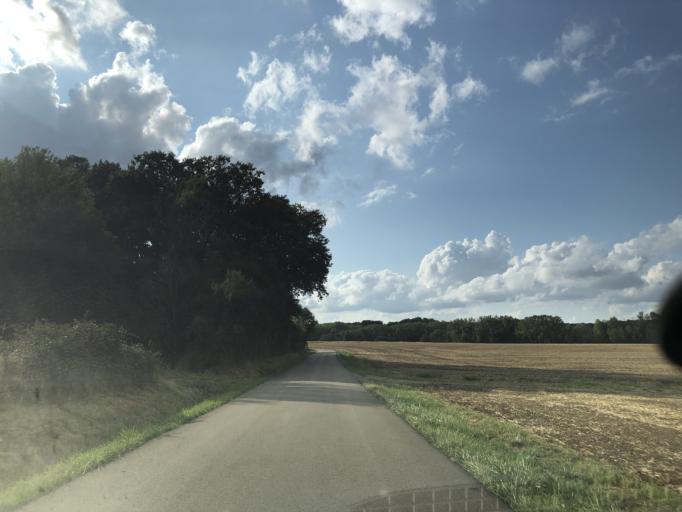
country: FR
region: Bourgogne
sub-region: Departement de l'Yonne
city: Charbuy
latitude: 47.8230
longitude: 3.4886
